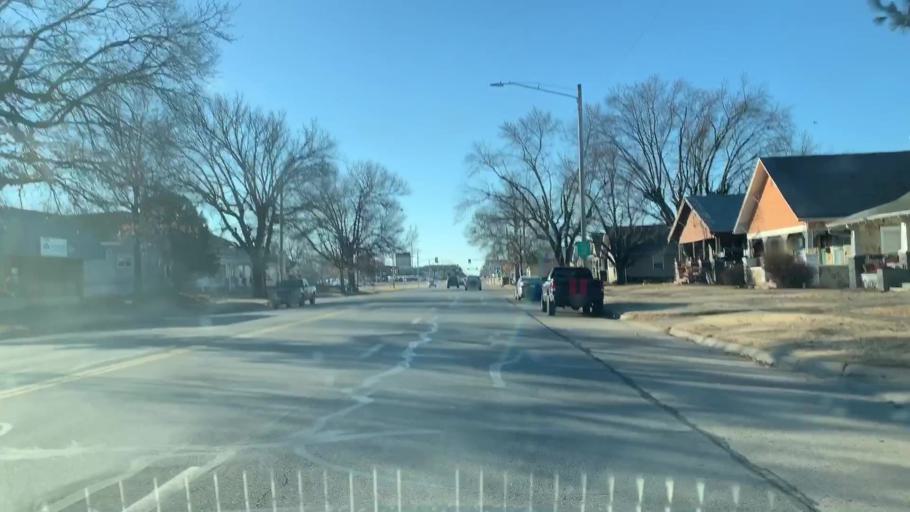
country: US
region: Kansas
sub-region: Crawford County
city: Pittsburg
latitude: 37.4218
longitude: -94.7050
